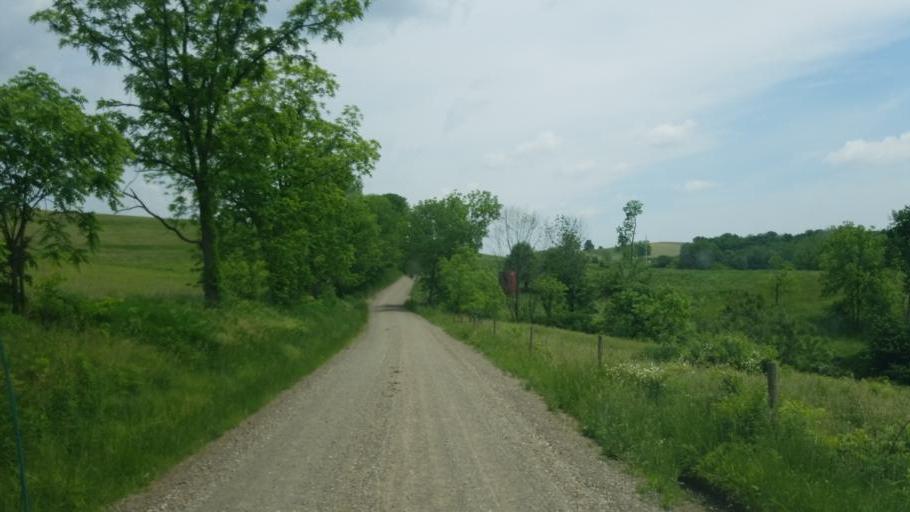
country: US
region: Ohio
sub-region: Holmes County
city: Millersburg
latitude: 40.4835
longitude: -81.8022
